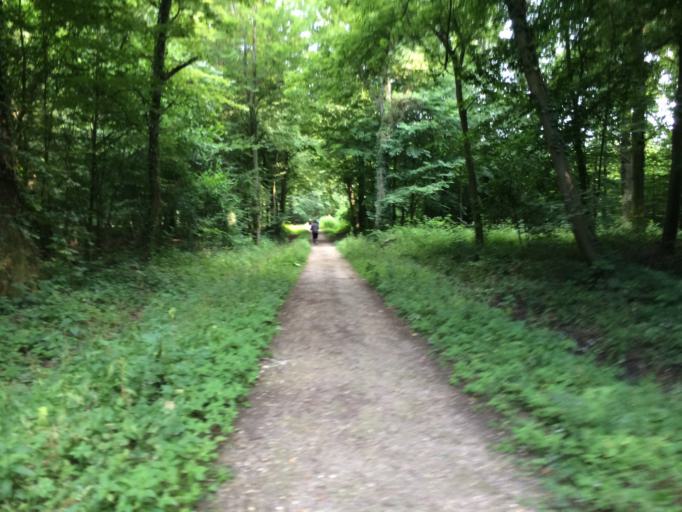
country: FR
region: Ile-de-France
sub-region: Departement de l'Essonne
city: Bievres
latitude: 48.7723
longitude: 2.2363
